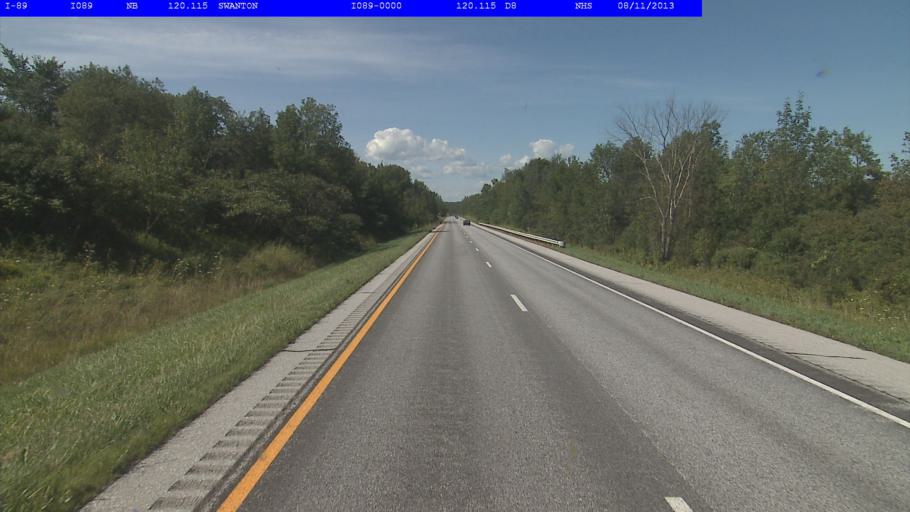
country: US
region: Vermont
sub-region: Franklin County
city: Swanton
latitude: 44.8787
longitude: -73.0834
